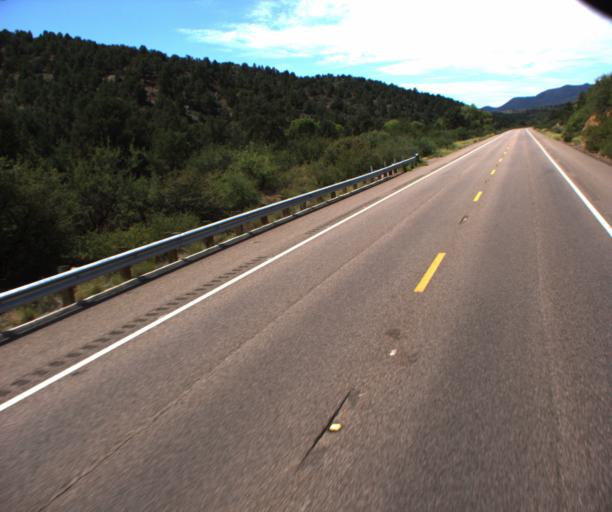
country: US
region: Arizona
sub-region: Gila County
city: Globe
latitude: 33.5700
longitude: -110.6641
